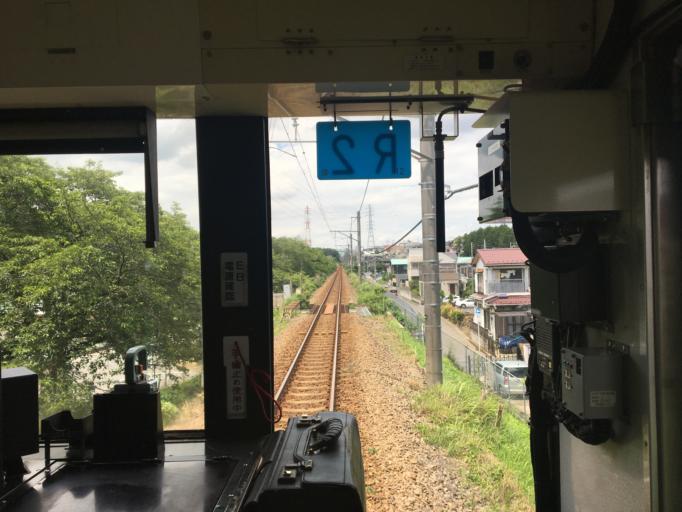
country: JP
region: Kanagawa
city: Zama
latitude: 35.5030
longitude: 139.3853
